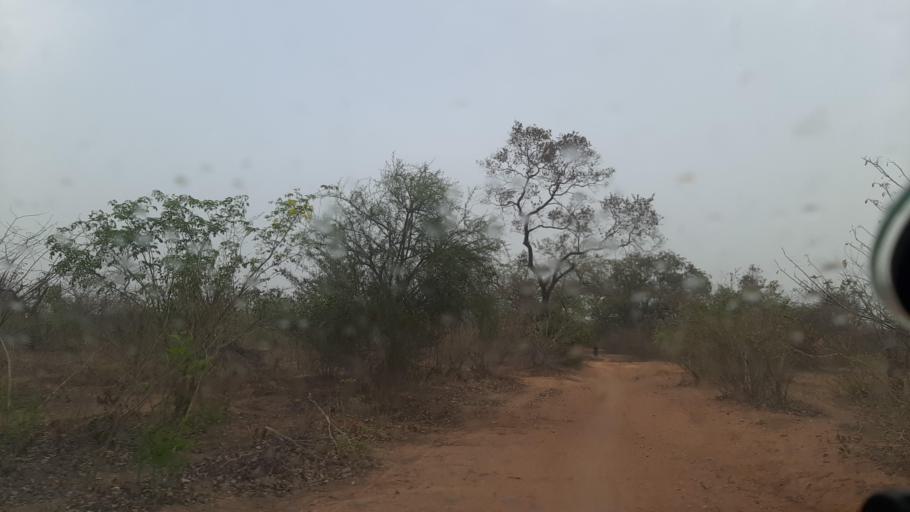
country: BF
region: Boucle du Mouhoun
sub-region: Province des Banwa
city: Salanso
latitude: 11.8634
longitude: -4.4396
